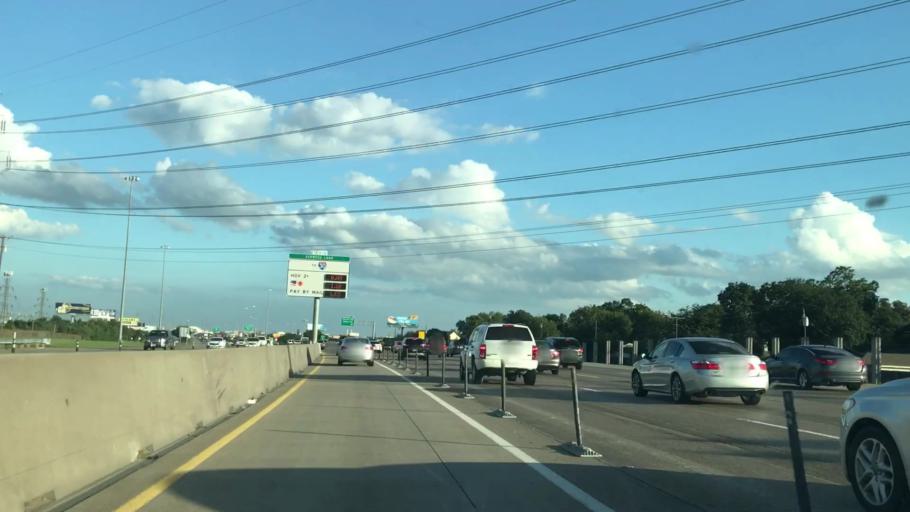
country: US
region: Texas
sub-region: Dallas County
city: Richardson
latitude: 32.8893
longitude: -96.7071
